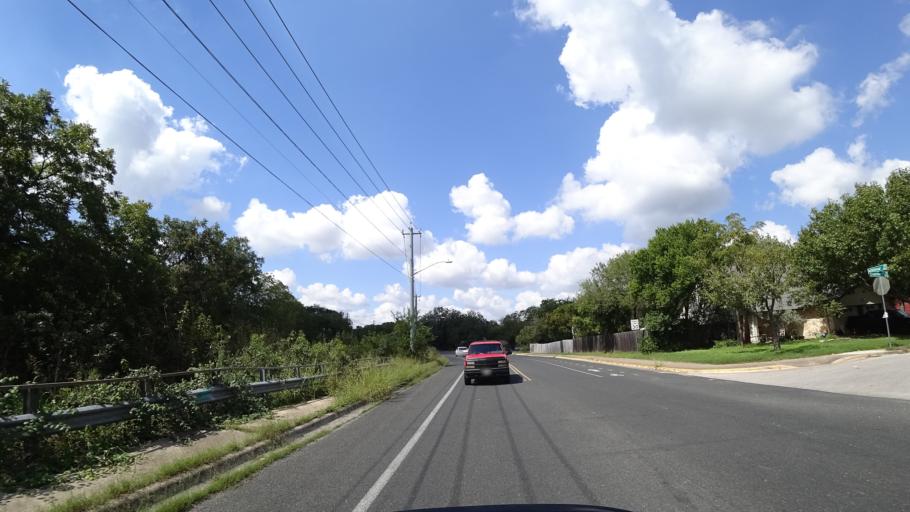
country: US
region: Texas
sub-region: Travis County
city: Onion Creek
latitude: 30.1831
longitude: -97.7855
